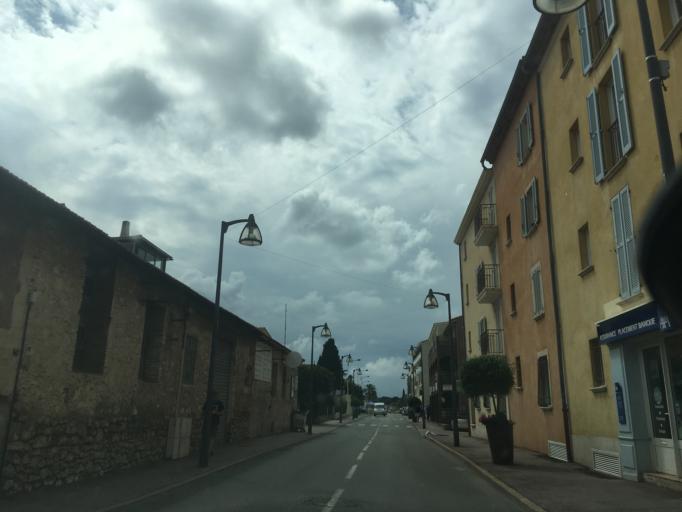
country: FR
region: Provence-Alpes-Cote d'Azur
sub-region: Departement du Var
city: La Londe-les-Maures
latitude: 43.1371
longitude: 6.2351
